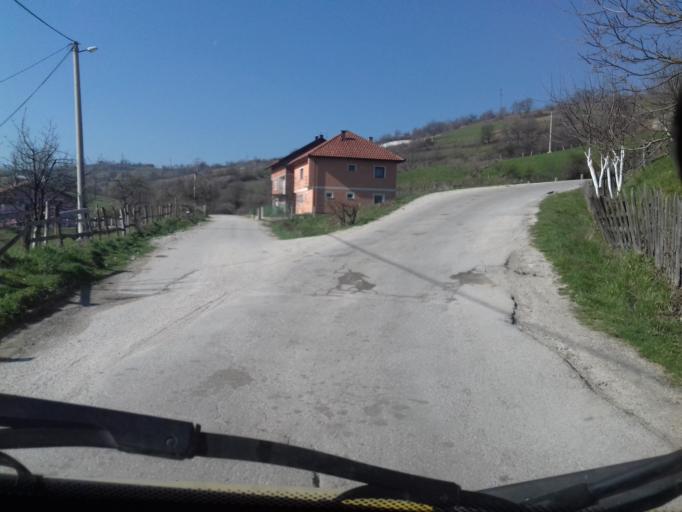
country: BA
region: Federation of Bosnia and Herzegovina
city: Travnik
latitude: 44.2509
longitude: 17.7449
